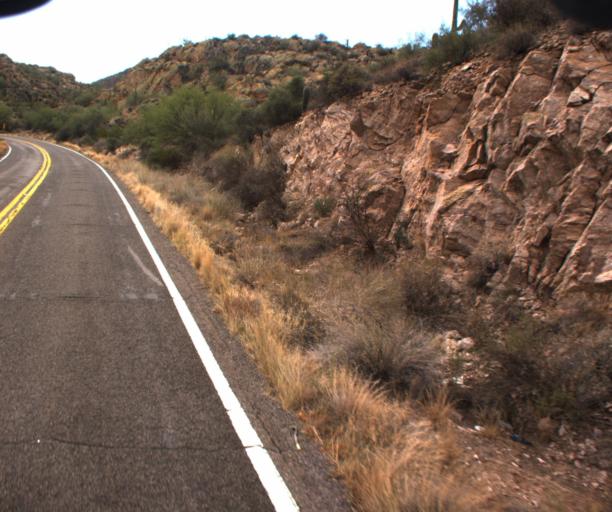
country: US
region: Arizona
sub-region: Pinal County
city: Apache Junction
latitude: 33.5310
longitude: -111.4543
